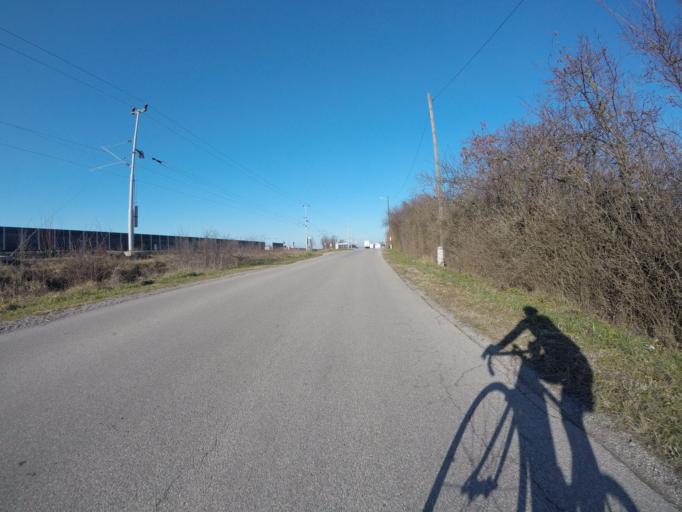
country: HR
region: Zagrebacka
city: Gradici
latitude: 45.7061
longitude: 16.0507
